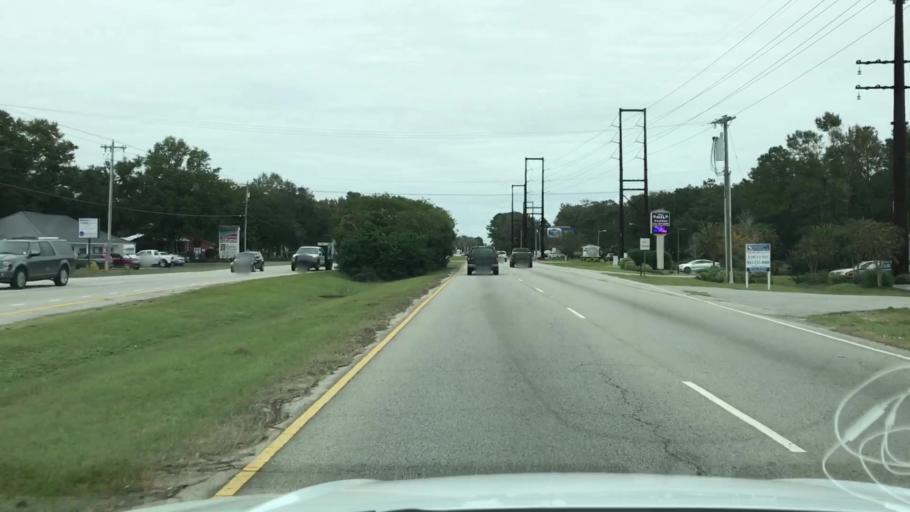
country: US
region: South Carolina
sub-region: Georgetown County
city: Murrells Inlet
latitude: 33.5504
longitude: -79.0478
